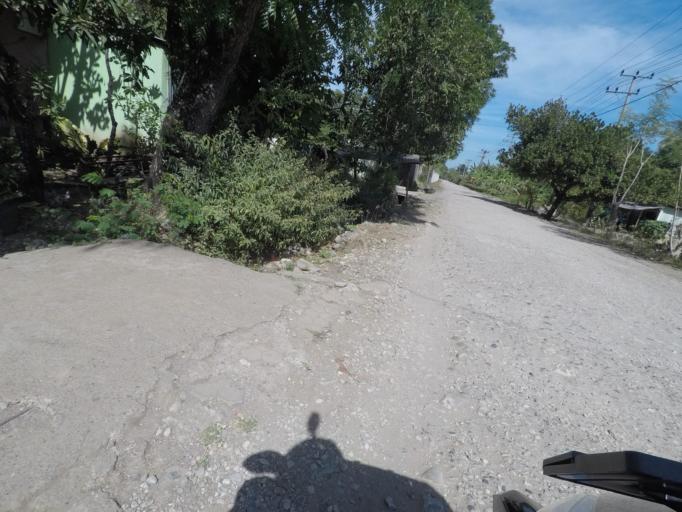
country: TL
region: Bobonaro
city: Maliana
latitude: -8.9882
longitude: 125.2188
